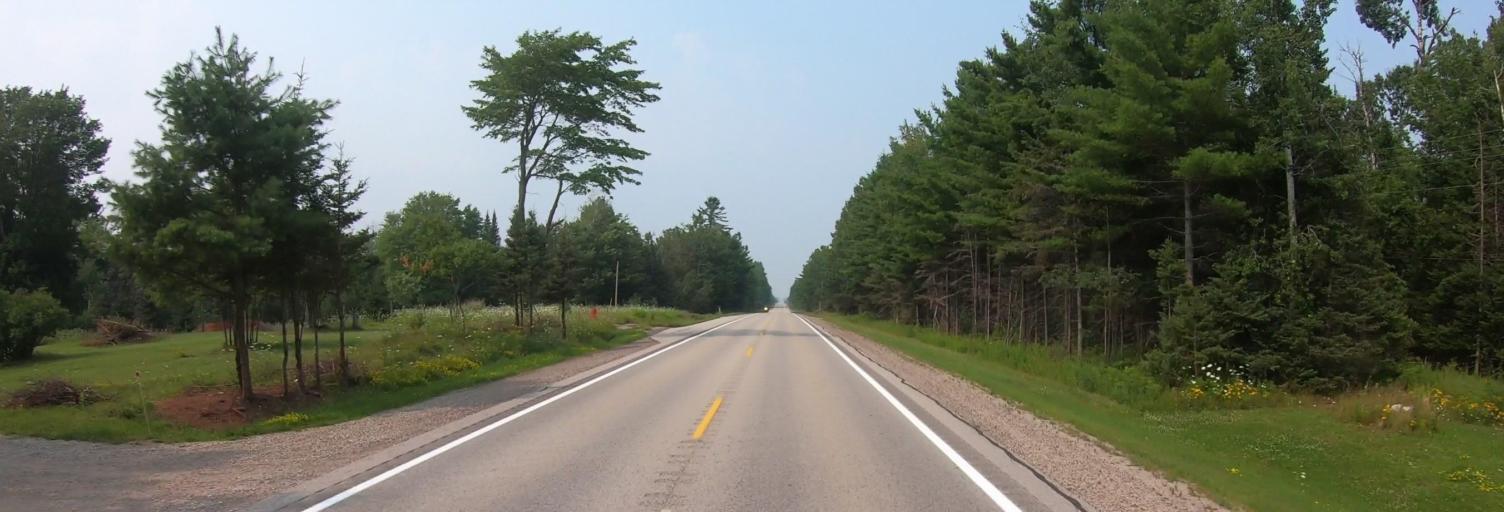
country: US
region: Michigan
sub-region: Chippewa County
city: Sault Ste. Marie
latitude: 46.2456
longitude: -84.3634
